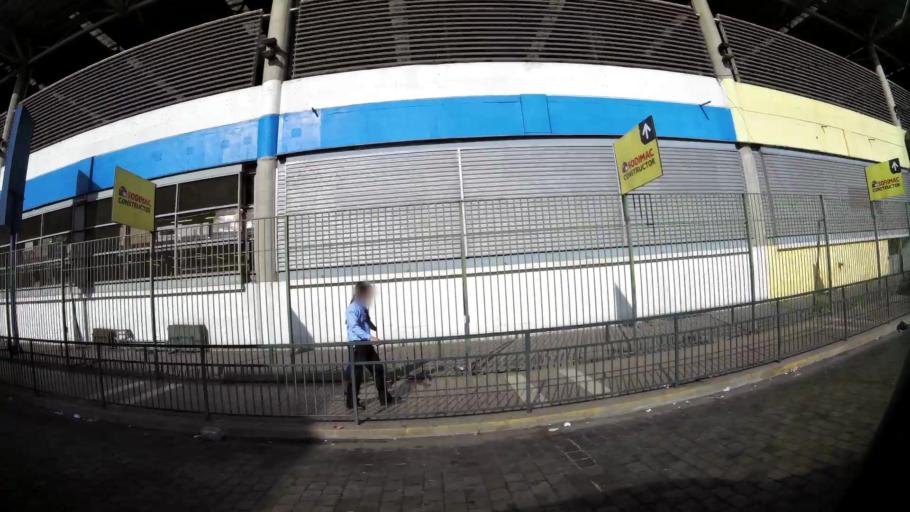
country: CL
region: Santiago Metropolitan
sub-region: Provincia de Santiago
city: Santiago
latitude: -33.4548
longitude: -70.6805
